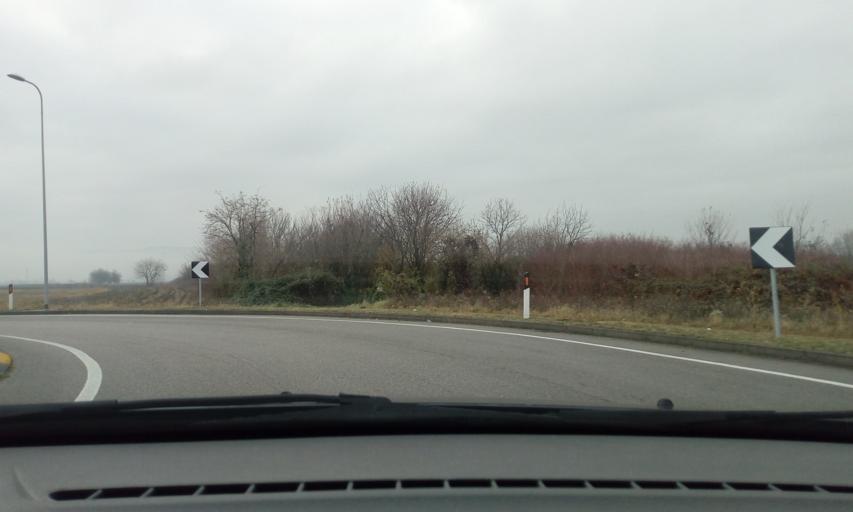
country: IT
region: Friuli Venezia Giulia
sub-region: Provincia di Gorizia
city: Mossa
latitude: 45.9284
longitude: 13.5463
